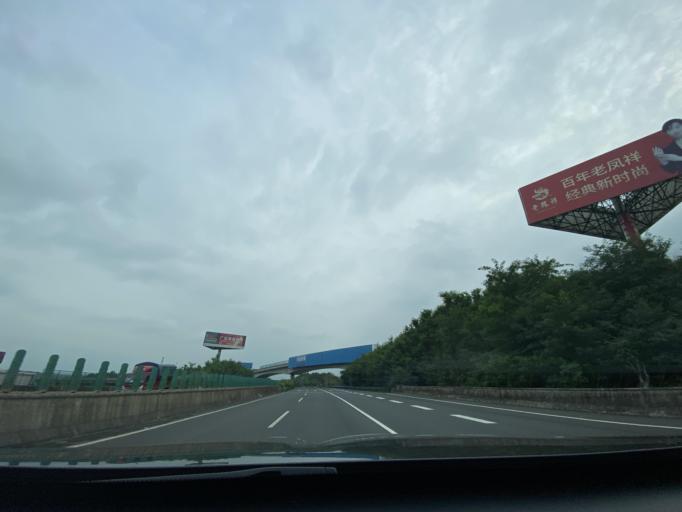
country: CN
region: Sichuan
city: Longquan
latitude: 30.5635
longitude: 104.4461
